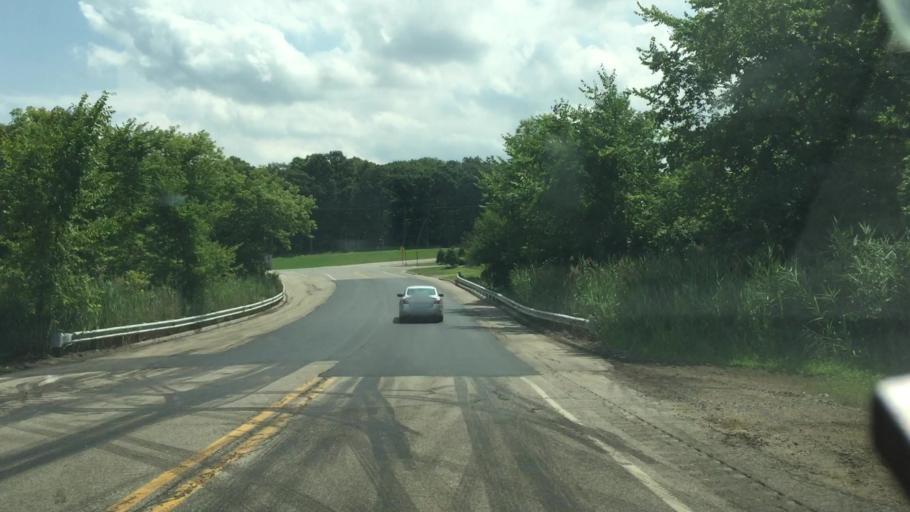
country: US
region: Michigan
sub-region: Oakland County
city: Auburn Hills
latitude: 42.6798
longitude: -83.2014
